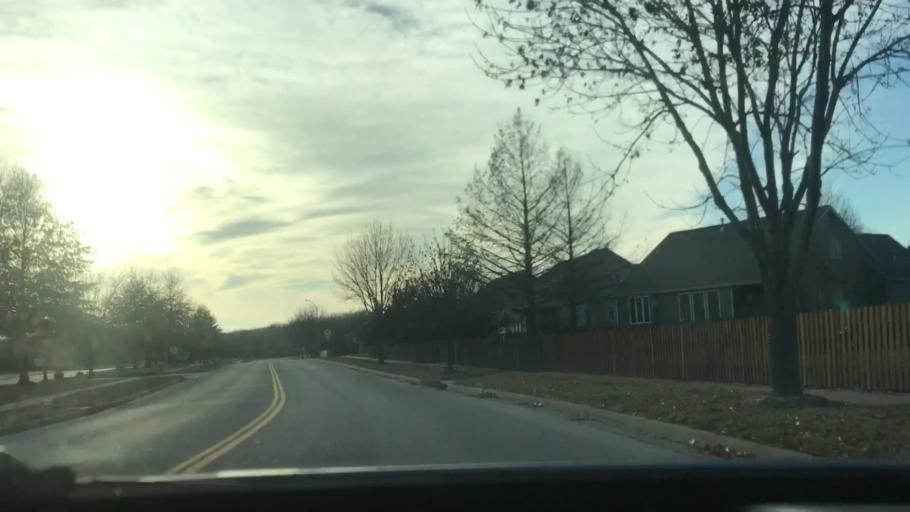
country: US
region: Missouri
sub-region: Jackson County
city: East Independence
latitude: 39.0185
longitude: -94.3711
